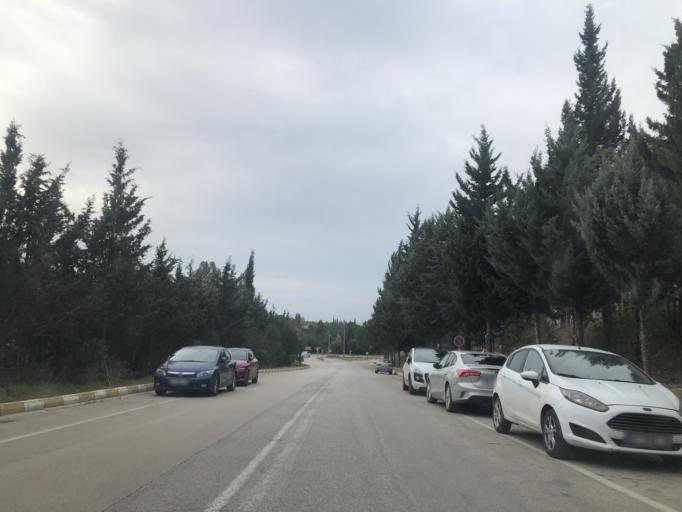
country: TR
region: Adana
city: Adana
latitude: 37.0591
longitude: 35.3528
